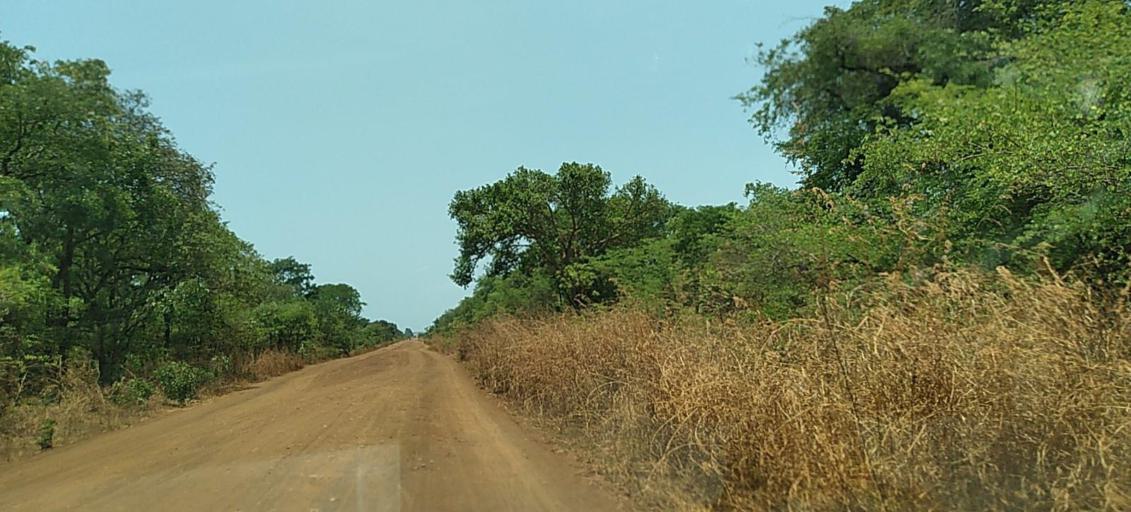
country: ZM
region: Copperbelt
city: Mpongwe
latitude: -13.6878
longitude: 27.8607
